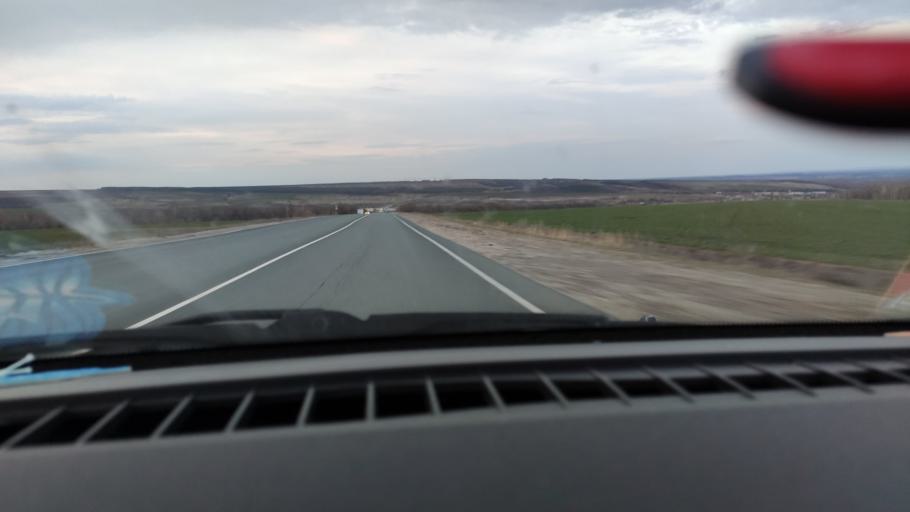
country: RU
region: Saratov
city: Sinodskoye
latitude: 51.9109
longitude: 46.5534
